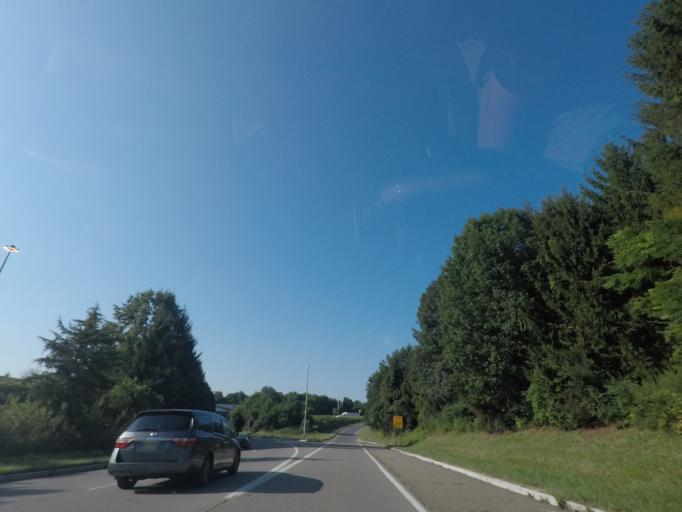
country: US
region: New Jersey
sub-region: Warren County
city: Alpha
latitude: 40.6705
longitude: -75.1378
